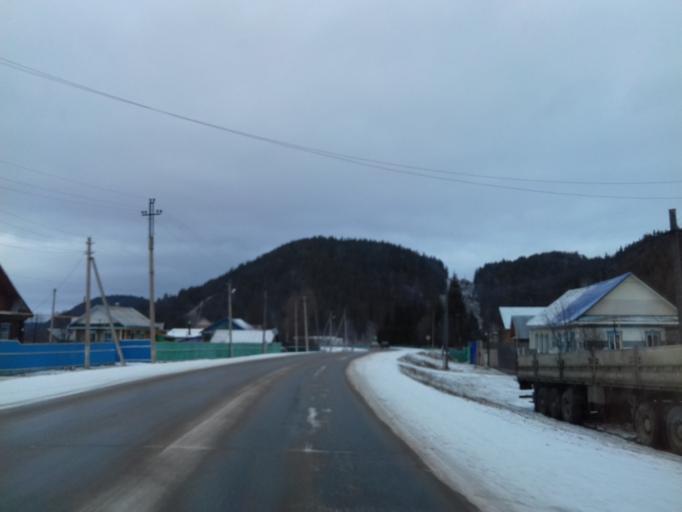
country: RU
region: Bashkortostan
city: Starosubkhangulovo
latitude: 53.1196
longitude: 57.4226
